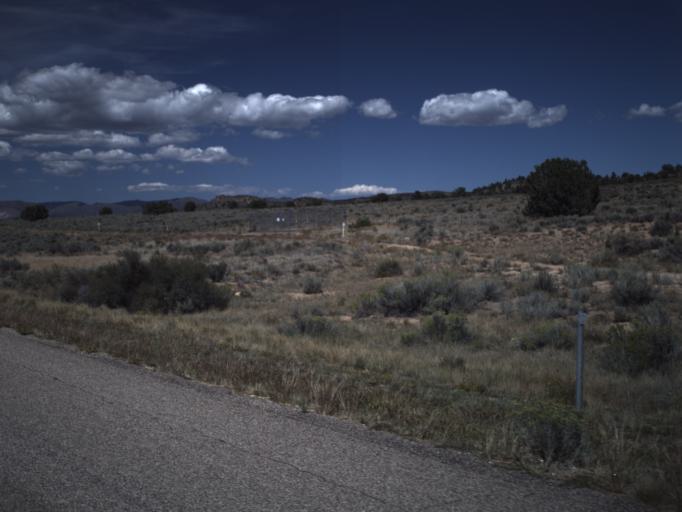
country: US
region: Utah
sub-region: Washington County
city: Ivins
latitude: 37.2760
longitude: -113.6484
